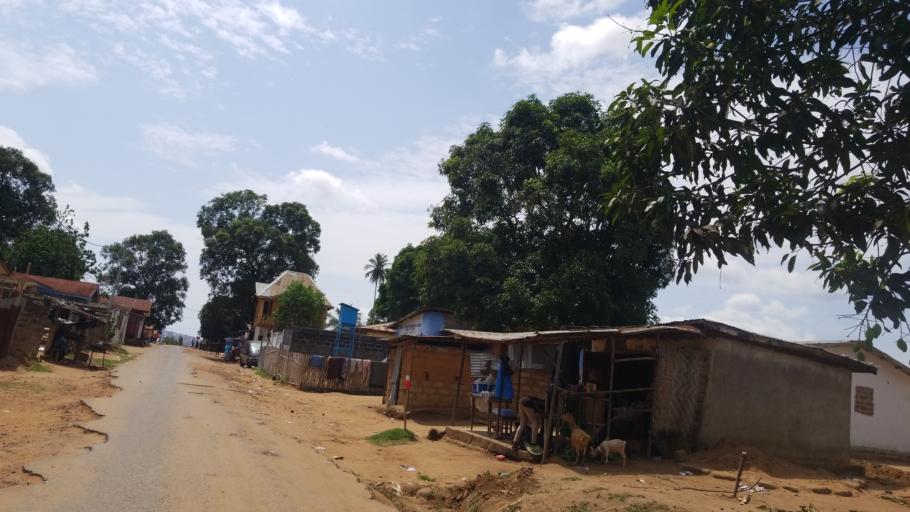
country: SL
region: Western Area
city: Waterloo
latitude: 8.3132
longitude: -13.0554
